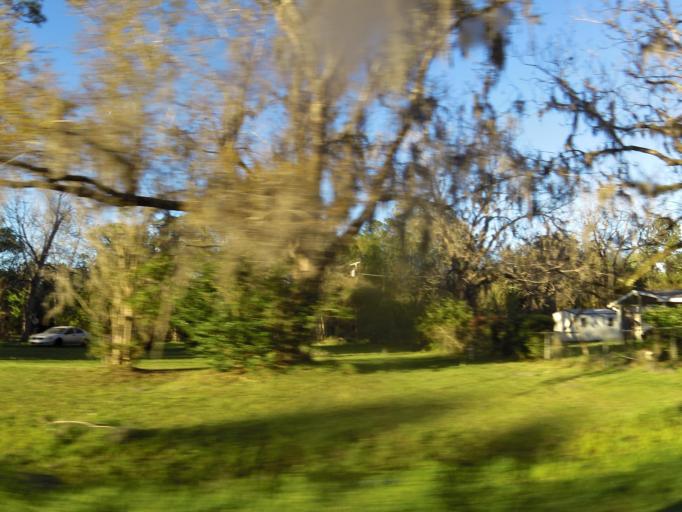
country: US
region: Florida
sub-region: Bradford County
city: Starke
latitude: 29.8639
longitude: -82.1215
